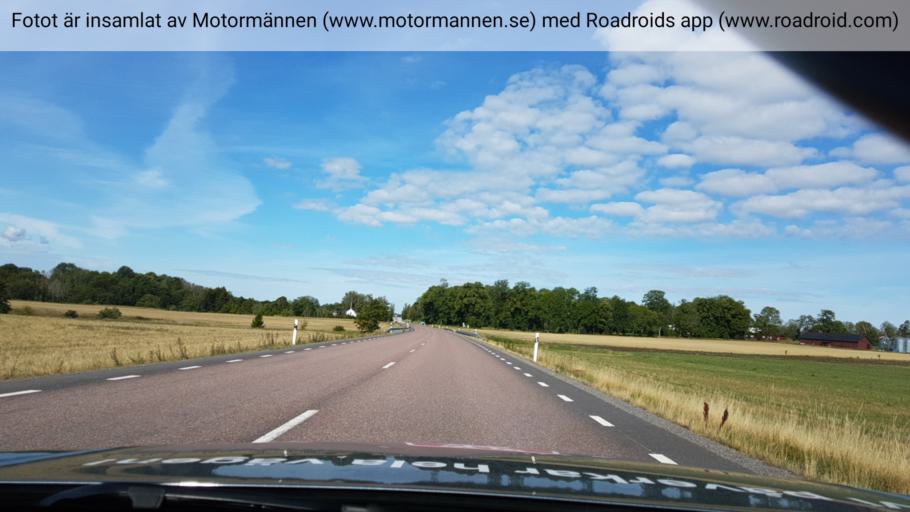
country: SE
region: Uppsala
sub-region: Osthammars Kommun
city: Bjorklinge
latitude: 59.9429
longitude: 17.4354
